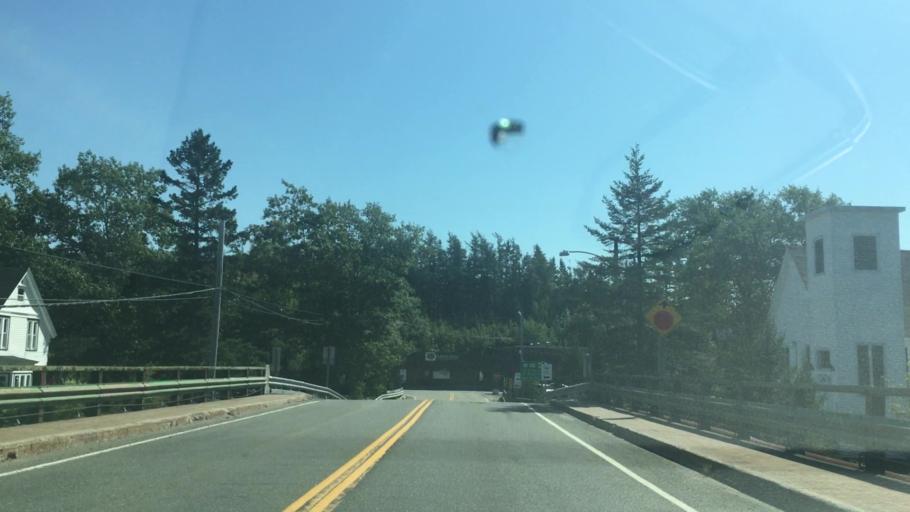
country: CA
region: Nova Scotia
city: Antigonish
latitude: 45.1431
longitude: -61.9839
